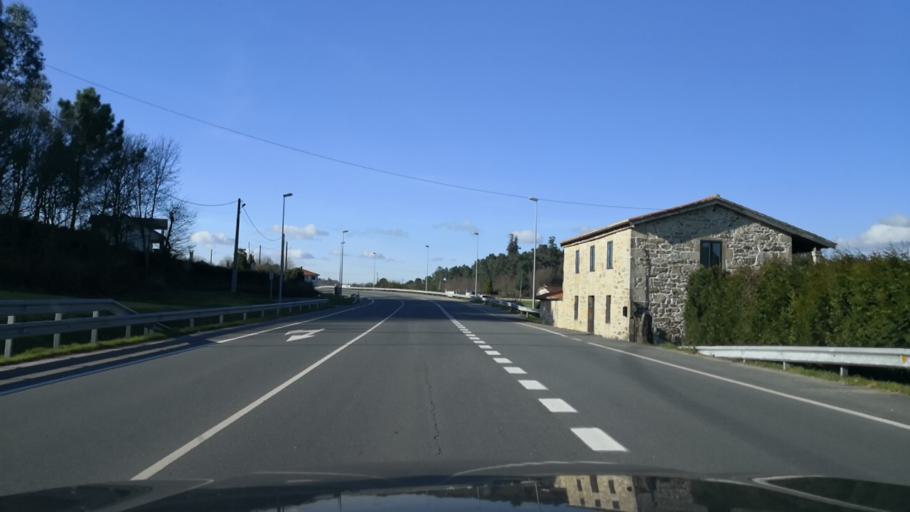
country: ES
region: Galicia
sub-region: Provincia de Pontevedra
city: Silleda
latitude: 42.7198
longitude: -8.2846
